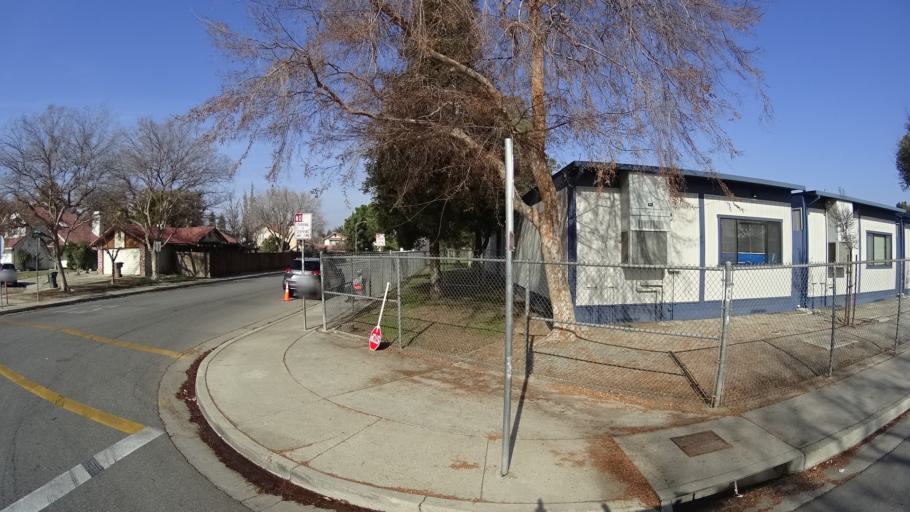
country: US
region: California
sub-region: Kern County
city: Bakersfield
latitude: 35.3197
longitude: -119.0512
